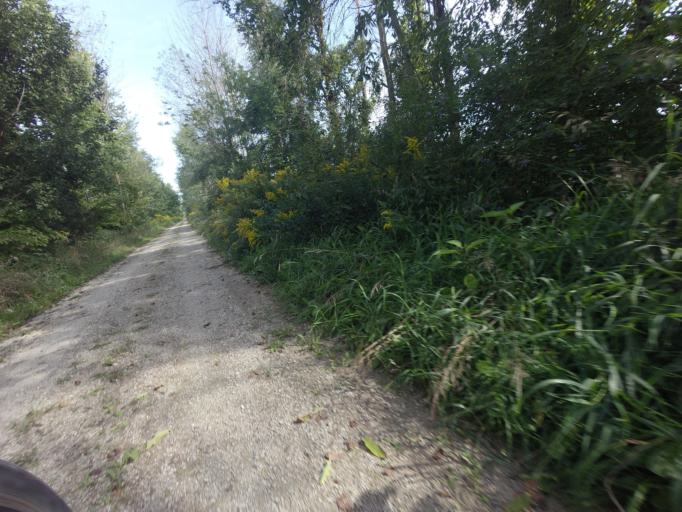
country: CA
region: Ontario
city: Waterloo
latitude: 43.5845
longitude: -80.4191
